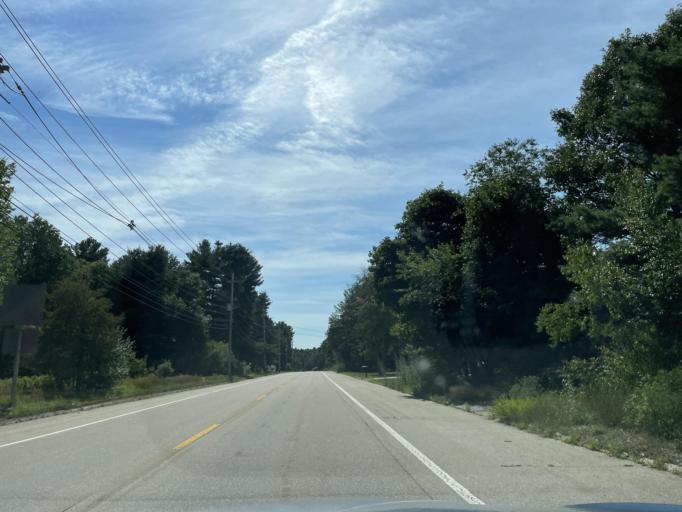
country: US
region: Massachusetts
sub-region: Norfolk County
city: Wrentham
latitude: 42.0784
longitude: -71.2951
